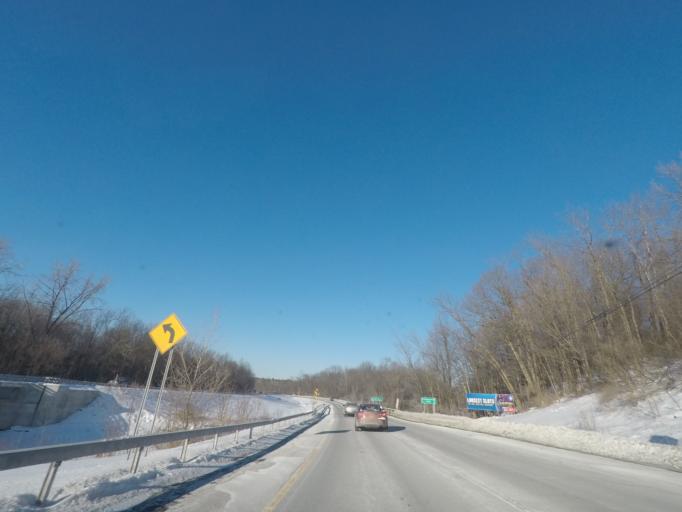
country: US
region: New York
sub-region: Saratoga County
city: Saratoga Springs
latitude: 43.0310
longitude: -73.7902
